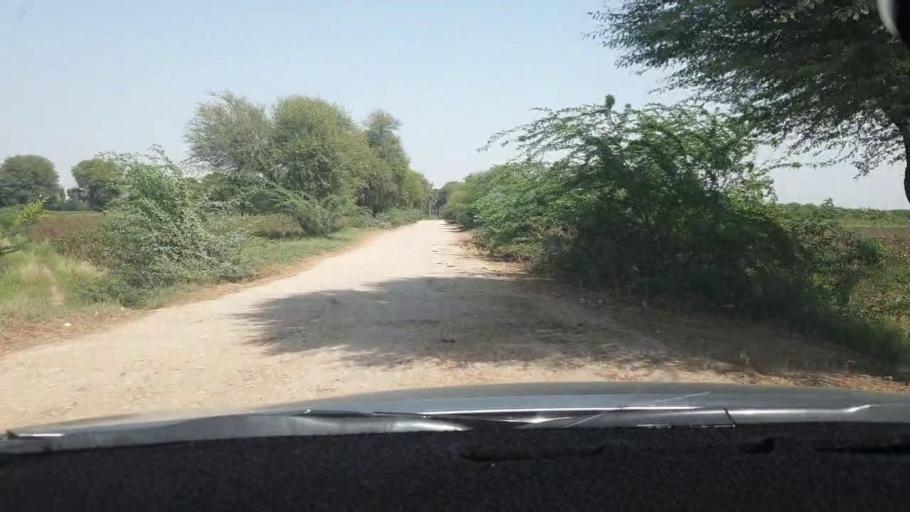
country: PK
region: Sindh
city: Tando Mittha Khan
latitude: 25.8464
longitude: 69.4401
